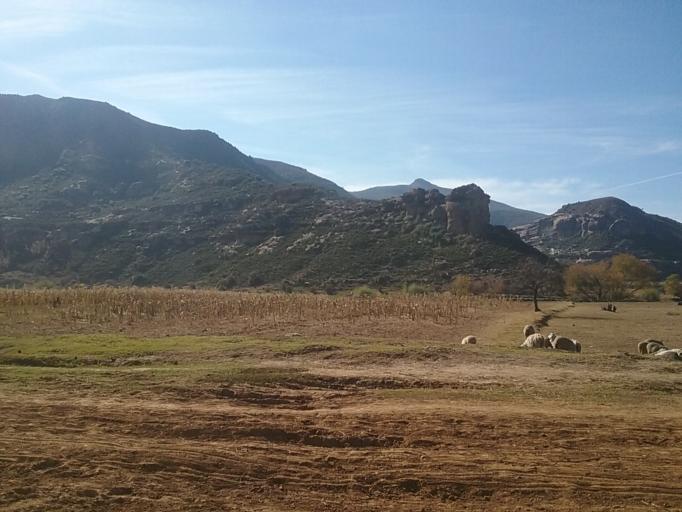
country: LS
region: Berea
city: Teyateyaneng
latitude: -29.2518
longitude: 27.9195
